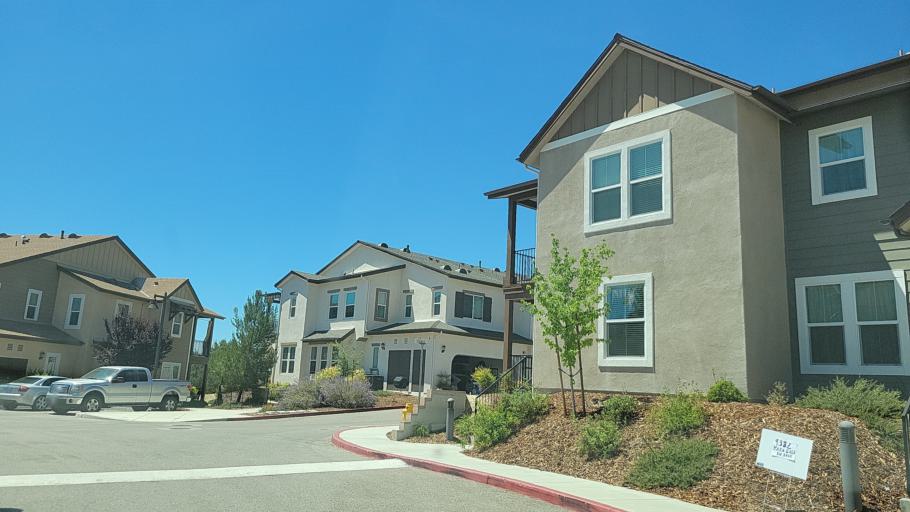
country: US
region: California
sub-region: San Luis Obispo County
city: Atascadero
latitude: 35.4564
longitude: -120.6285
